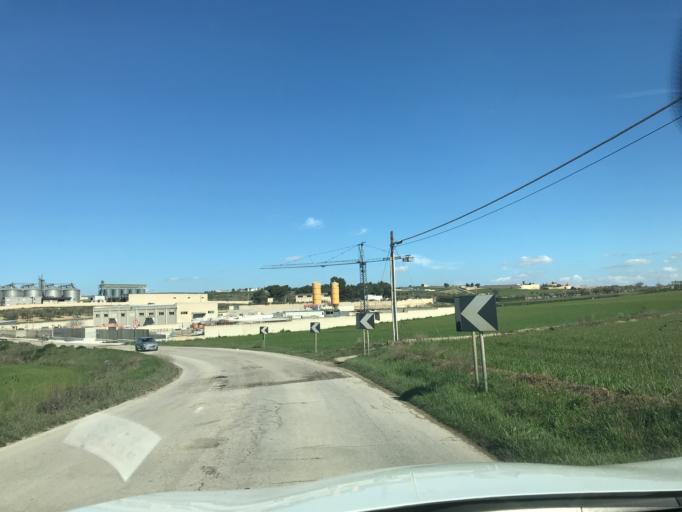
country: IT
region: Apulia
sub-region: Provincia di Bari
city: Gravina in Puglia
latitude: 40.8377
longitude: 16.4267
